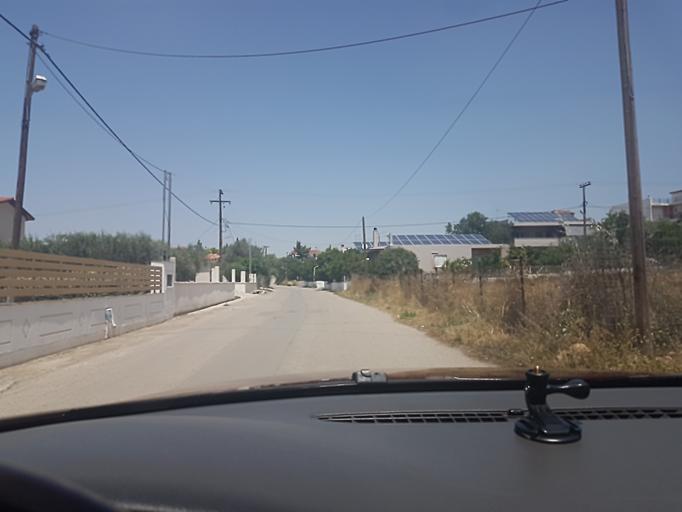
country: GR
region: Central Greece
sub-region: Nomos Evvoias
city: Vasilikon
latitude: 38.4207
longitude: 23.6677
